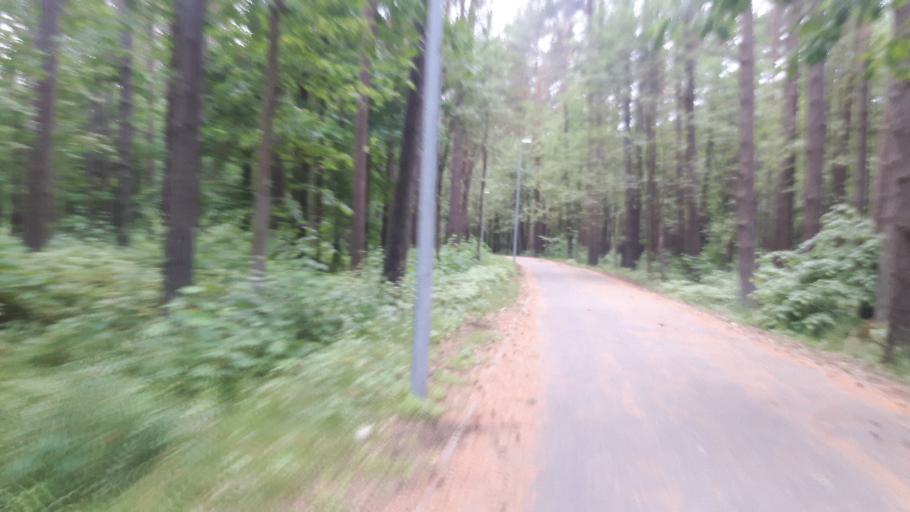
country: LV
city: Tireli
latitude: 56.9569
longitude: 23.6401
